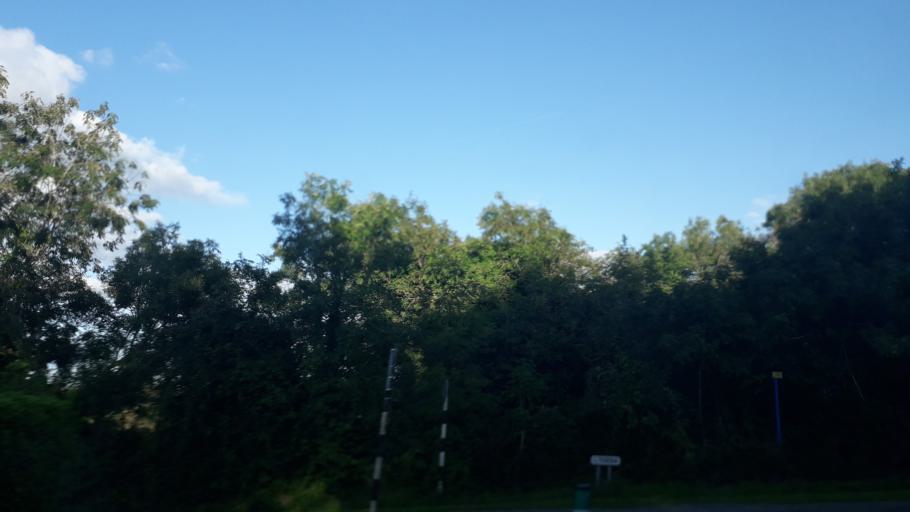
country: IE
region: Leinster
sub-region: Lu
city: Carlingford
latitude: 54.0217
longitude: -6.1470
